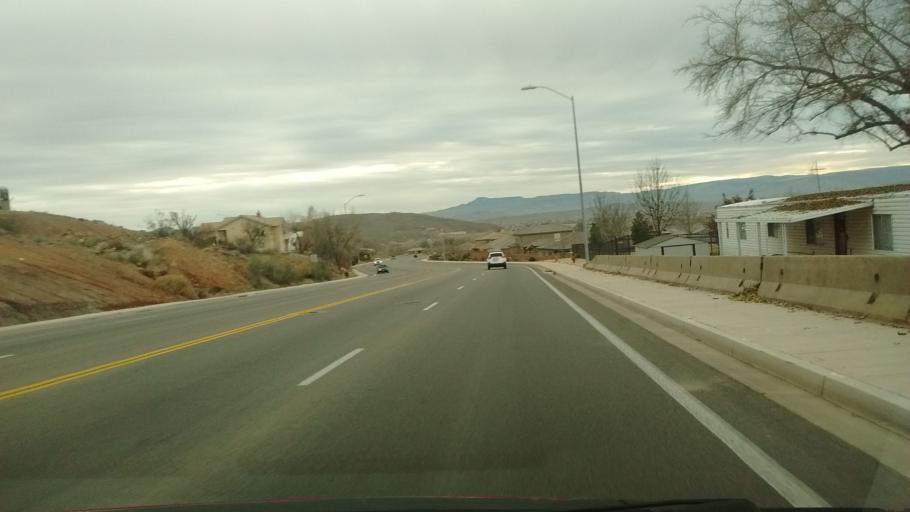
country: US
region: Utah
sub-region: Washington County
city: Washington
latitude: 37.1248
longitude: -113.5054
